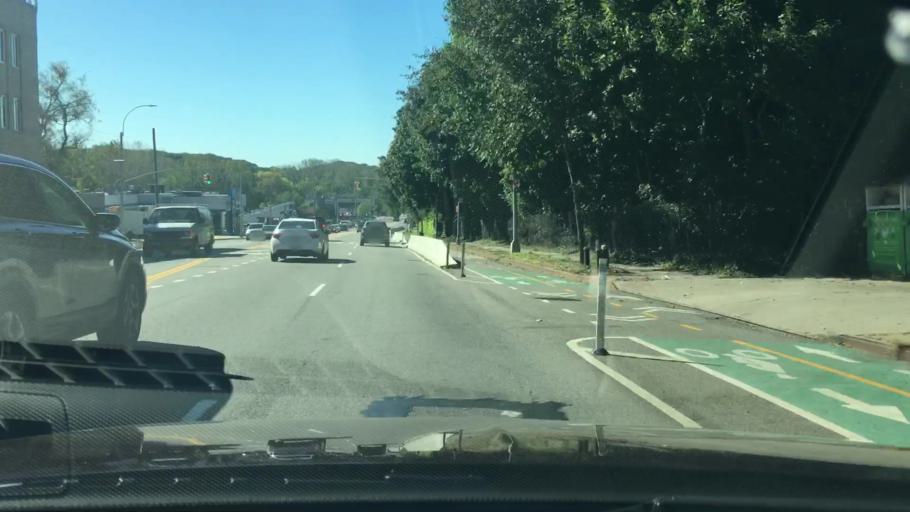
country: US
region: New York
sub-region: Nassau County
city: Great Neck Estates
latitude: 40.7653
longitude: -73.7450
